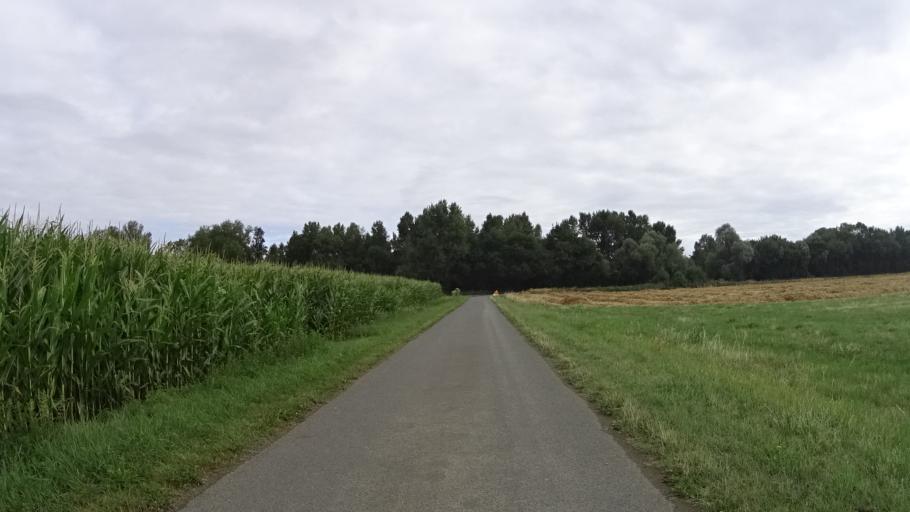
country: FR
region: Pays de la Loire
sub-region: Departement de Maine-et-Loire
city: Saint-Germain-des-Pres
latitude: 47.3776
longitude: -0.8075
